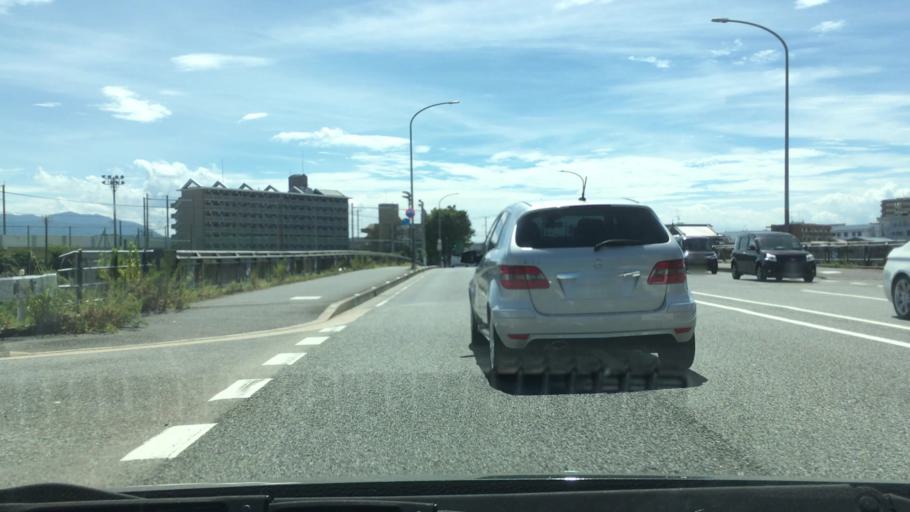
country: JP
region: Fukuoka
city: Fukuoka-shi
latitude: 33.5631
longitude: 130.4326
